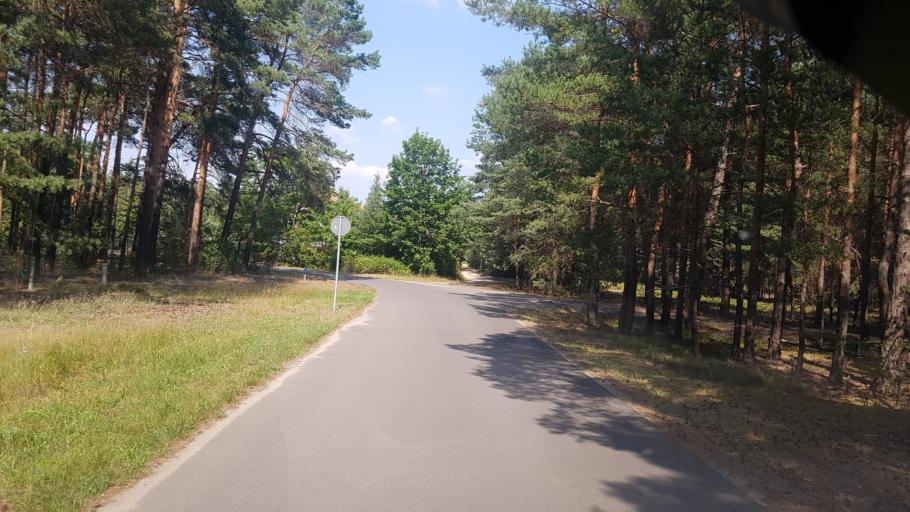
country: DE
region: Brandenburg
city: Spremberg
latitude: 51.6303
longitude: 14.4041
